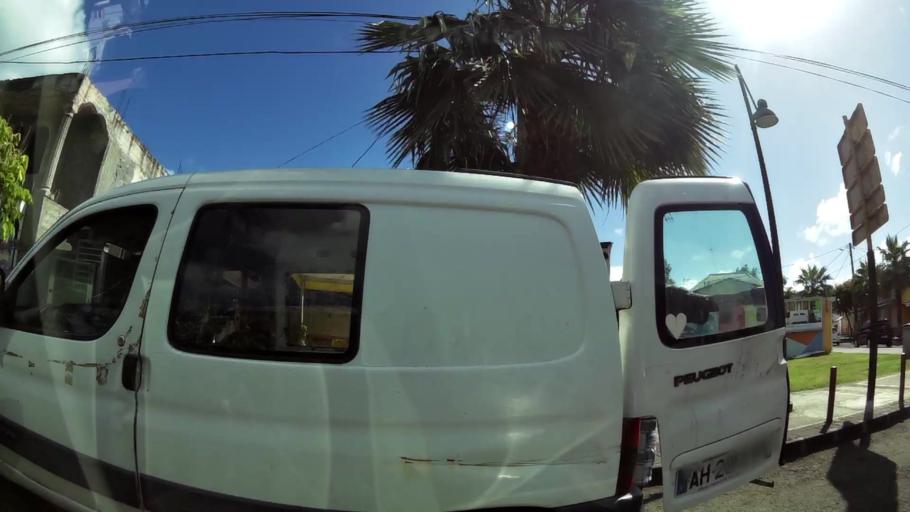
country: GP
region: Guadeloupe
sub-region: Guadeloupe
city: Saint-Francois
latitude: 16.2521
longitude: -61.2732
